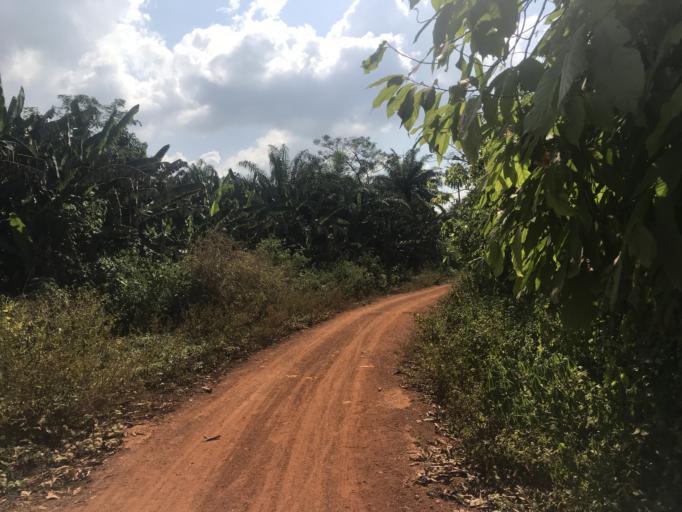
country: NG
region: Osun
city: Ibokun
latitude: 7.8138
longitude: 4.6969
